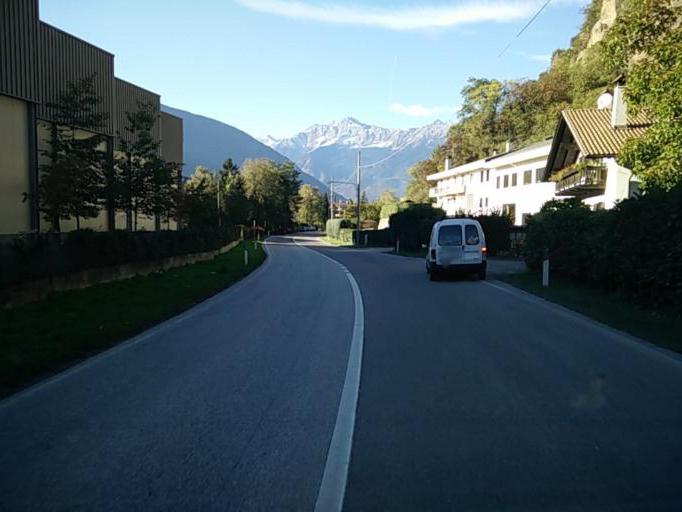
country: IT
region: Trentino-Alto Adige
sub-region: Bolzano
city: Sinigo
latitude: 46.6270
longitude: 11.1834
